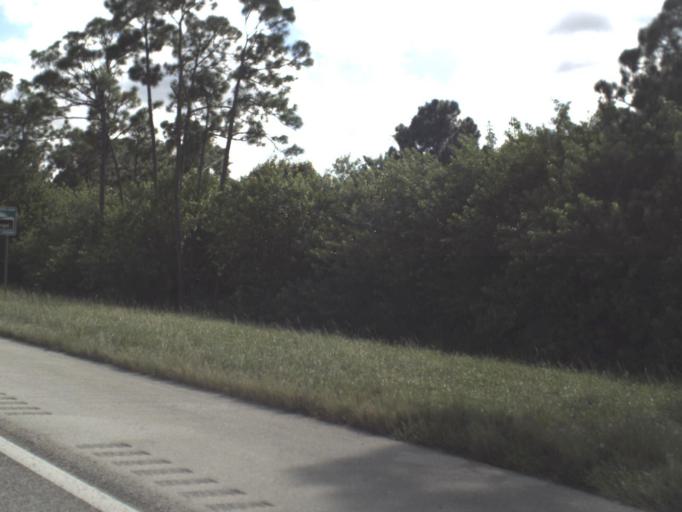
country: US
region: Florida
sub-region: Saint Lucie County
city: Port Saint Lucie
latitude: 27.2268
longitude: -80.3416
